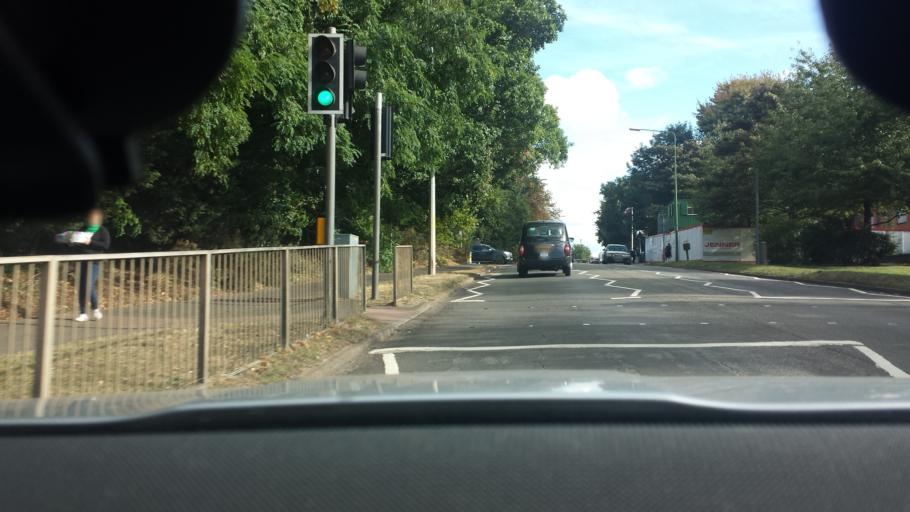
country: GB
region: England
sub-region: Kent
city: Swanley
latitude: 51.3990
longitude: 0.1702
